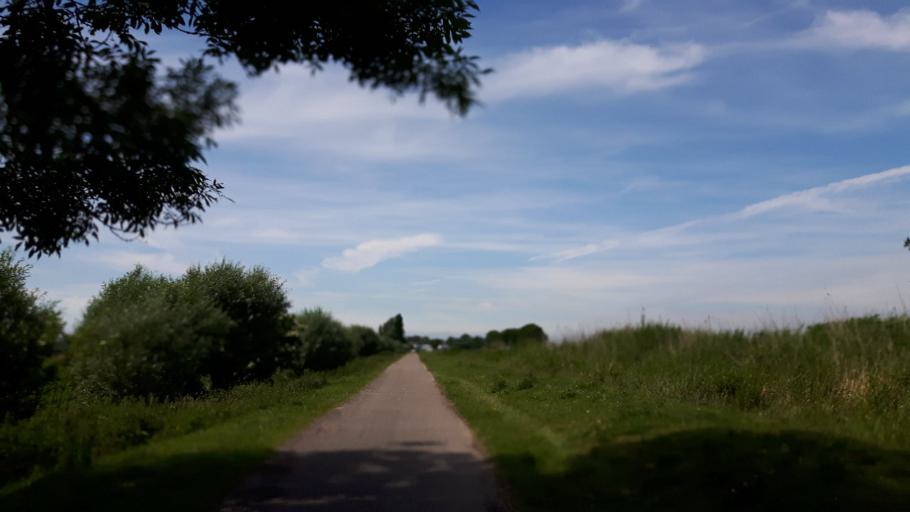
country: NL
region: North Holland
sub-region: Gemeente Aalsmeer
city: Aalsmeer
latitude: 52.2069
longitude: 4.7324
